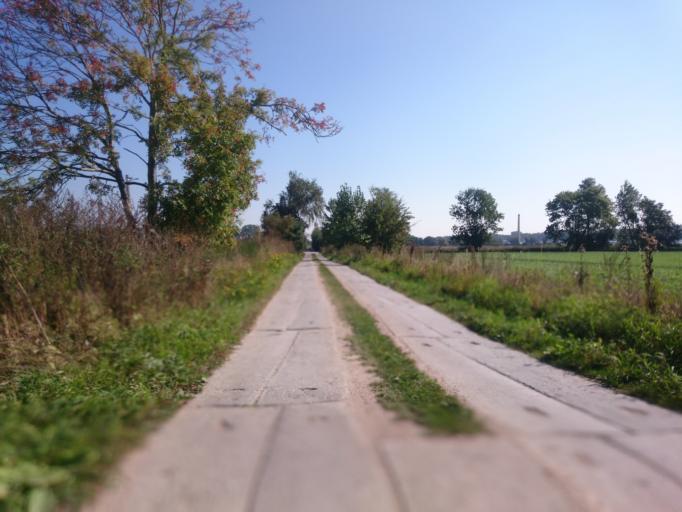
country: DE
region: Mecklenburg-Vorpommern
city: Barth
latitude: 54.3581
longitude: 12.6948
